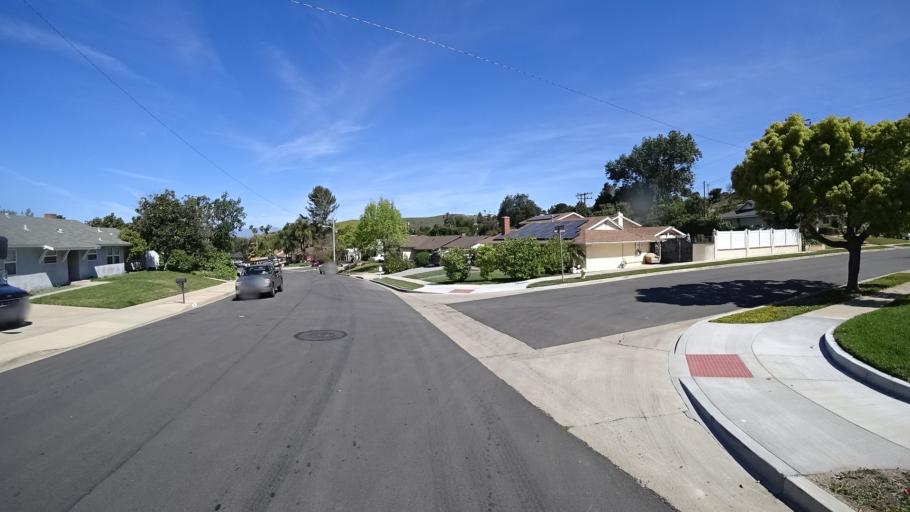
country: US
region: California
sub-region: Ventura County
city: Thousand Oaks
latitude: 34.2233
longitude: -118.8657
